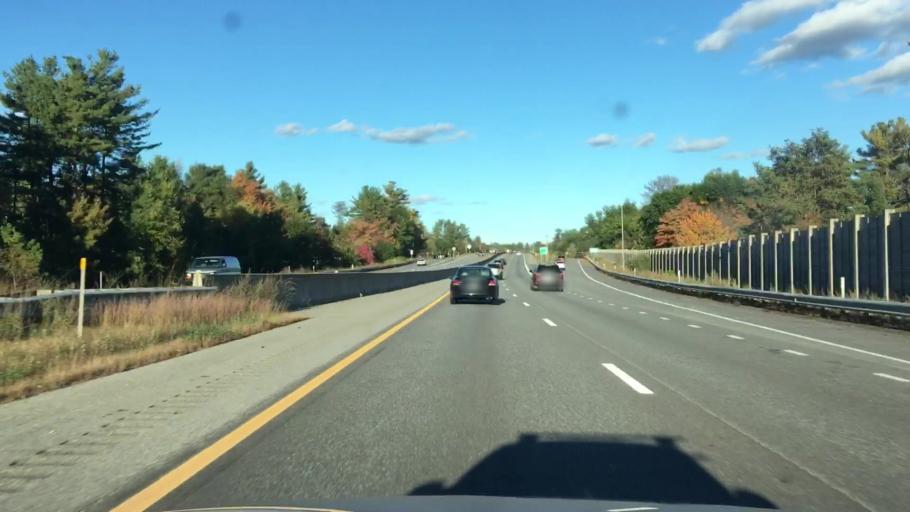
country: US
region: New Hampshire
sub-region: Merrimack County
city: South Hooksett
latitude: 43.0045
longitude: -71.4005
